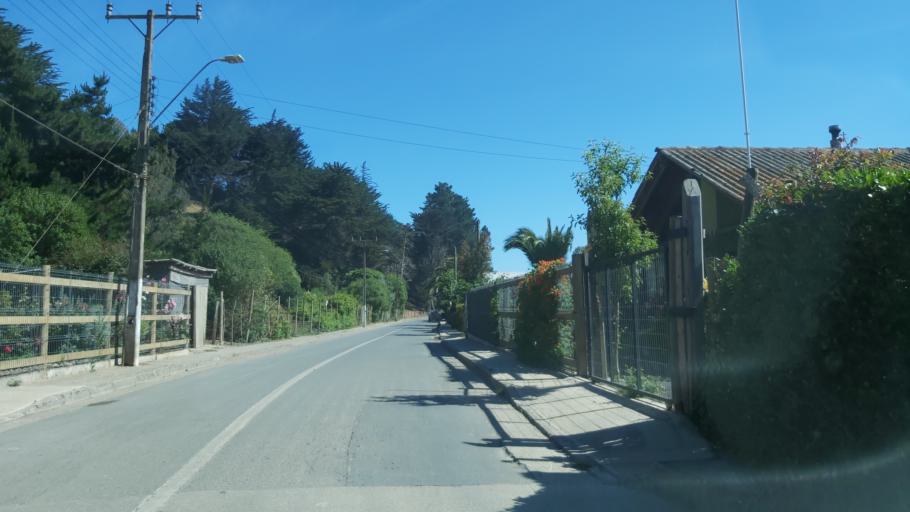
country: CL
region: Maule
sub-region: Provincia de Talca
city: Constitucion
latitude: -34.7591
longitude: -72.0829
